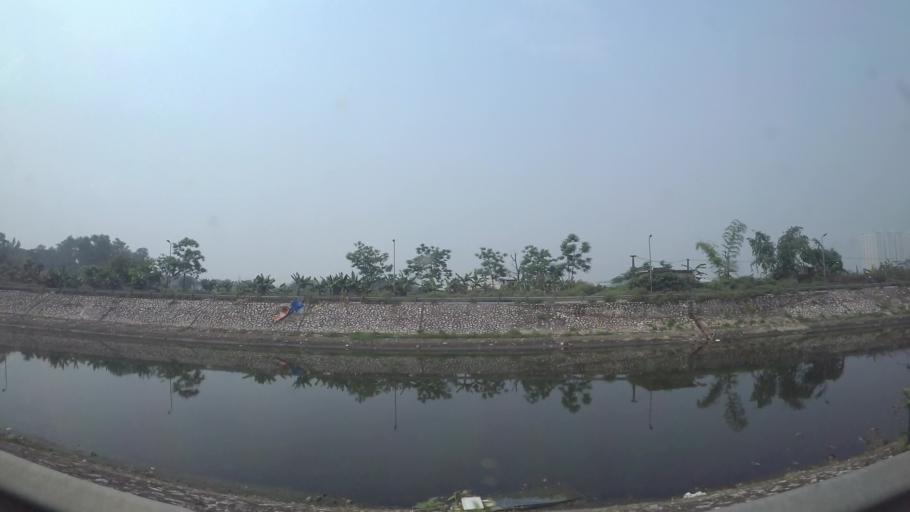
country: VN
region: Ha Noi
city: Van Dien
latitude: 20.9581
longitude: 105.8207
